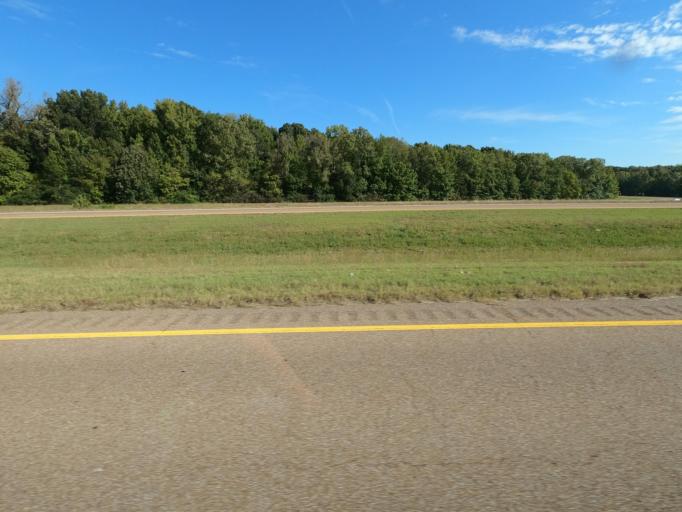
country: US
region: Tennessee
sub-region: Shelby County
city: Millington
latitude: 35.3204
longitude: -89.8758
